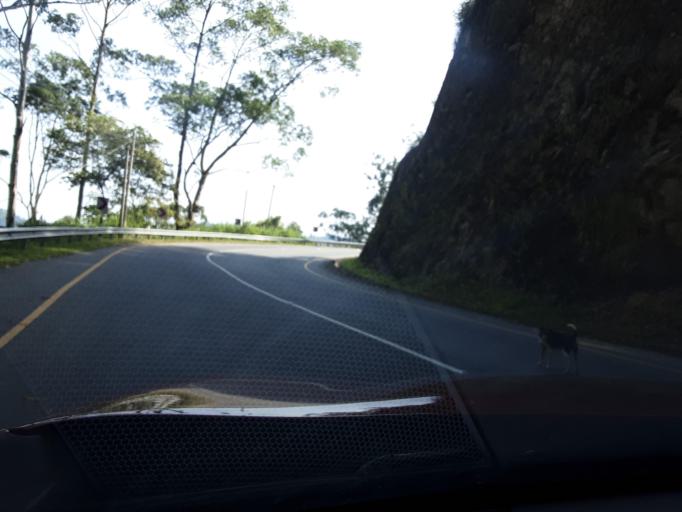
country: LK
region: Uva
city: Badulla
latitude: 6.9626
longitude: 81.0965
